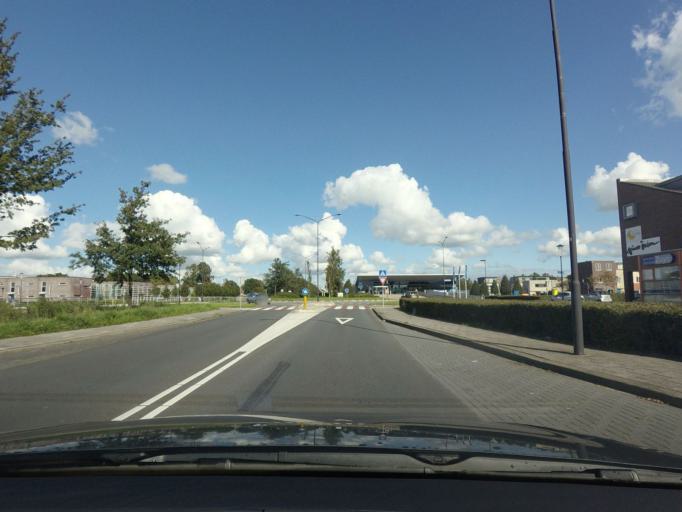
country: NL
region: North Holland
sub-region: Gemeente Langedijk
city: Broek op Langedijk
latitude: 52.6490
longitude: 4.8251
